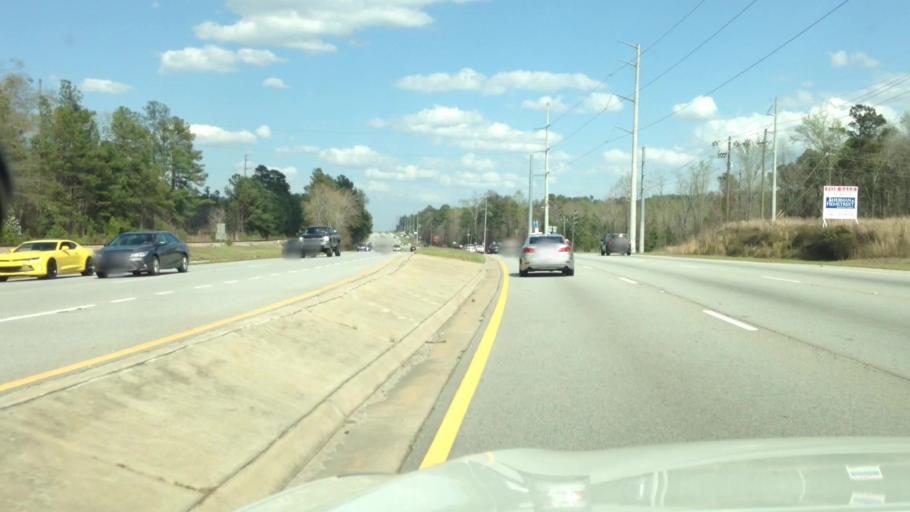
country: US
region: Georgia
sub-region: Columbia County
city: Martinez
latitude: 33.4398
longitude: -82.1099
